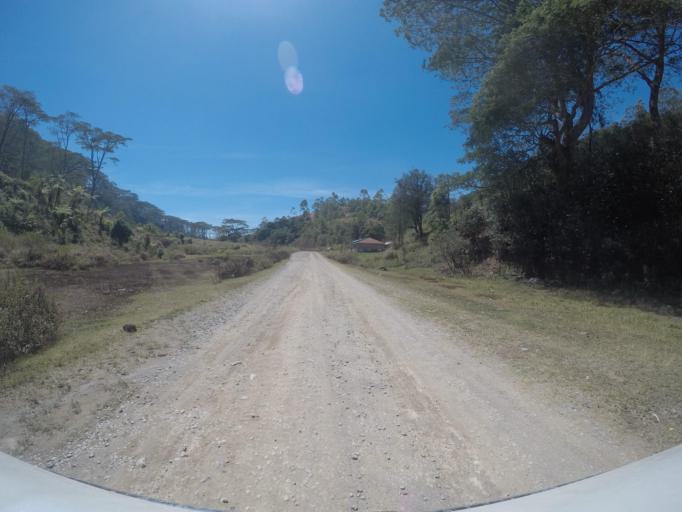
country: TL
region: Ermera
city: Gleno
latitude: -8.7757
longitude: 125.3908
